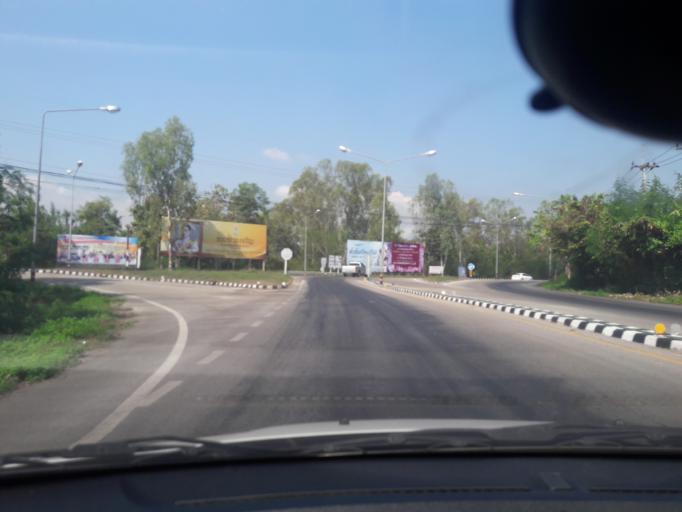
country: TH
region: Lampang
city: Lampang
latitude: 18.2211
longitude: 99.4909
